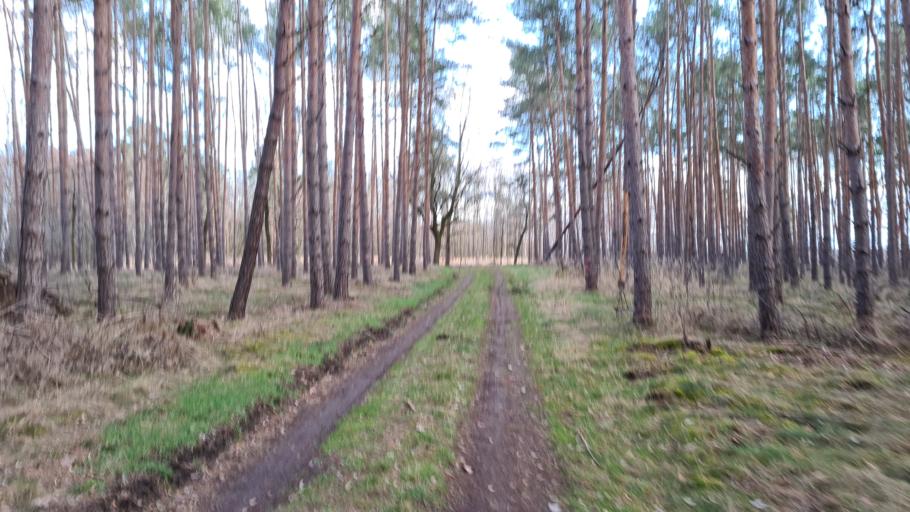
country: DE
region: Brandenburg
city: Falkenberg
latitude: 51.5758
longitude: 13.3152
